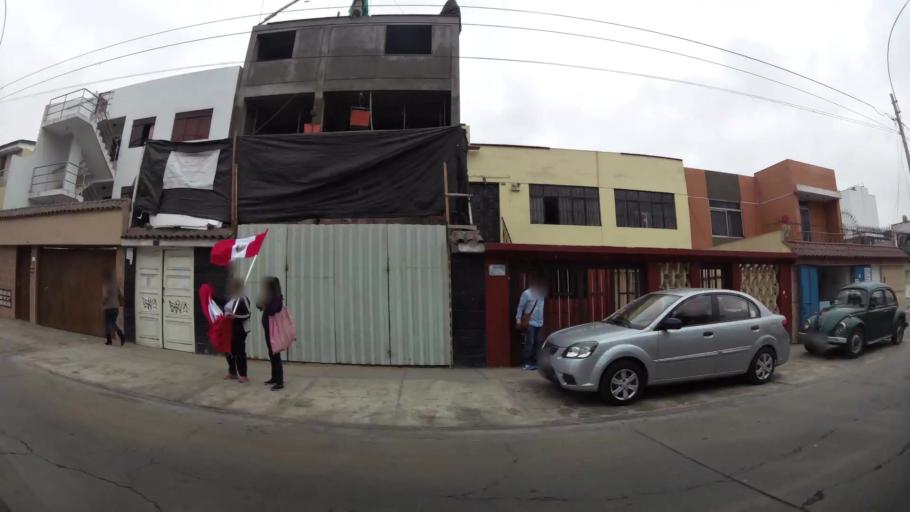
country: PE
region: Callao
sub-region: Callao
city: Callao
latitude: -12.0699
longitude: -77.0956
